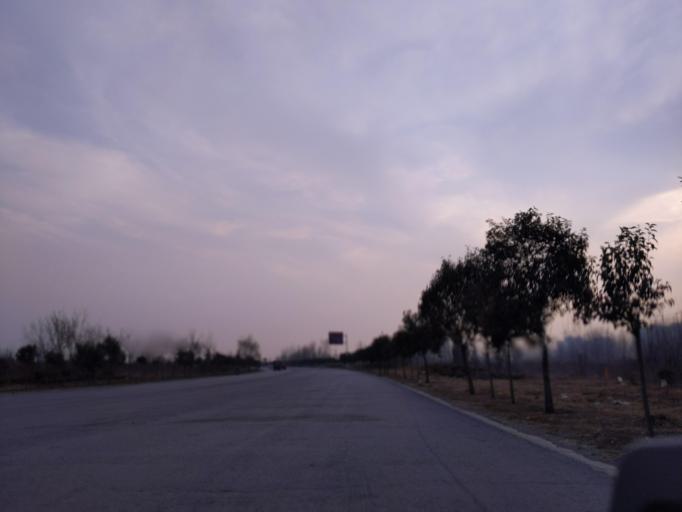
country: CN
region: Henan Sheng
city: Puyang
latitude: 35.8160
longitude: 114.9685
